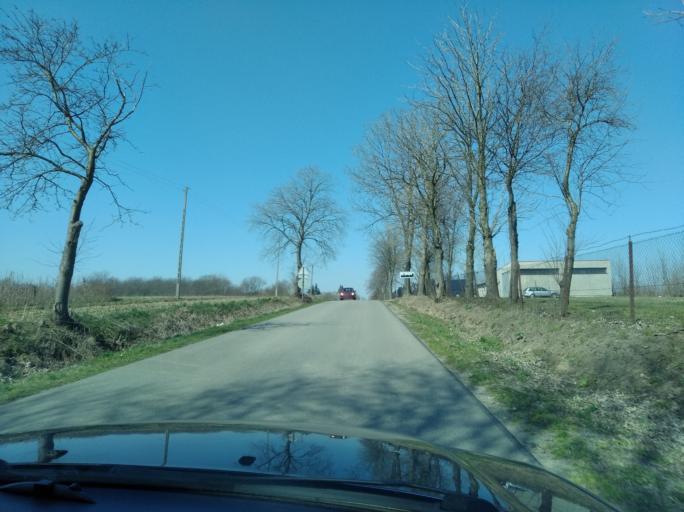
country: PL
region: Subcarpathian Voivodeship
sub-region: Powiat przeworski
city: Pantalowice
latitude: 49.9484
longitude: 22.4393
